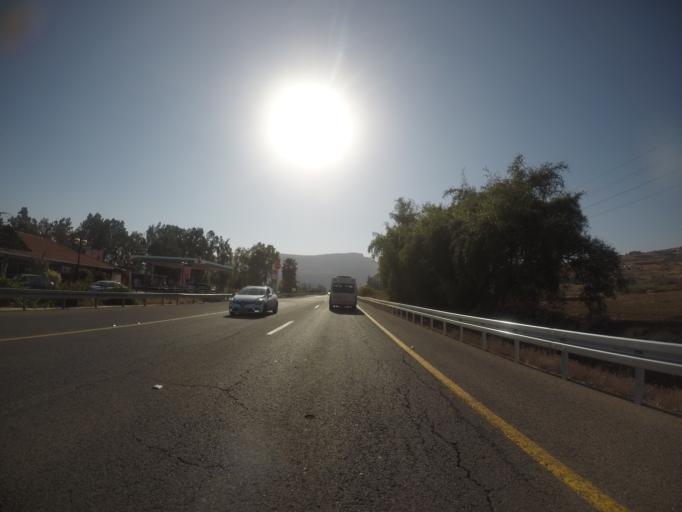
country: IL
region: Northern District
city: Tiberias
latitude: 32.8456
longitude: 35.5165
